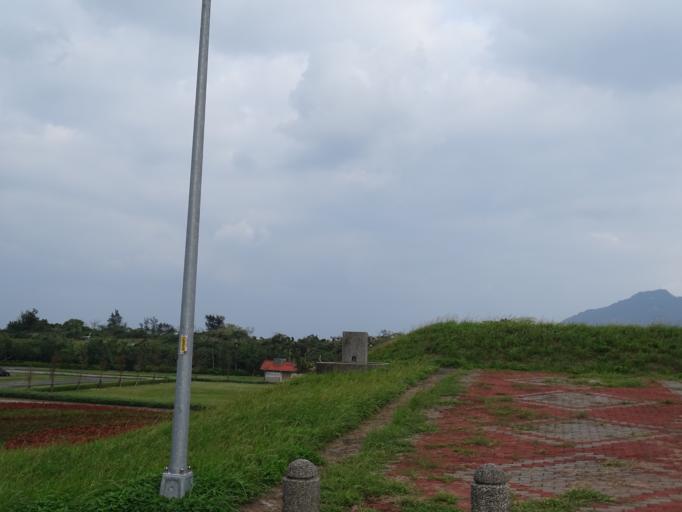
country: TW
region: Taiwan
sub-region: Keelung
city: Keelung
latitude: 25.0291
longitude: 121.9290
